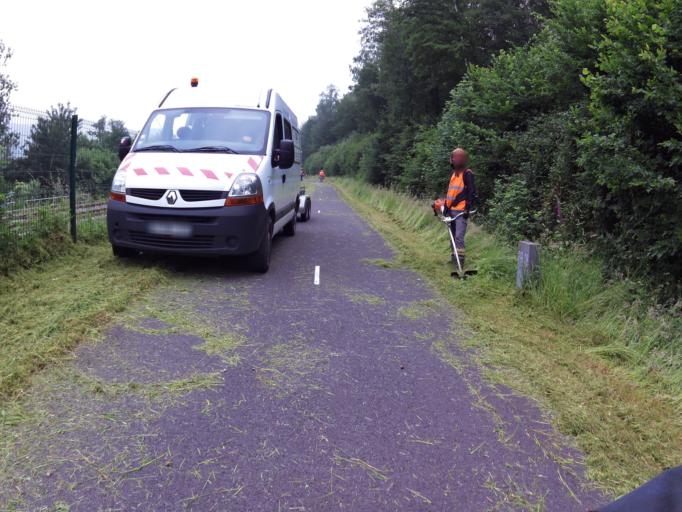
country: FR
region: Champagne-Ardenne
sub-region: Departement des Ardennes
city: Revin
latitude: 49.9639
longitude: 4.6626
